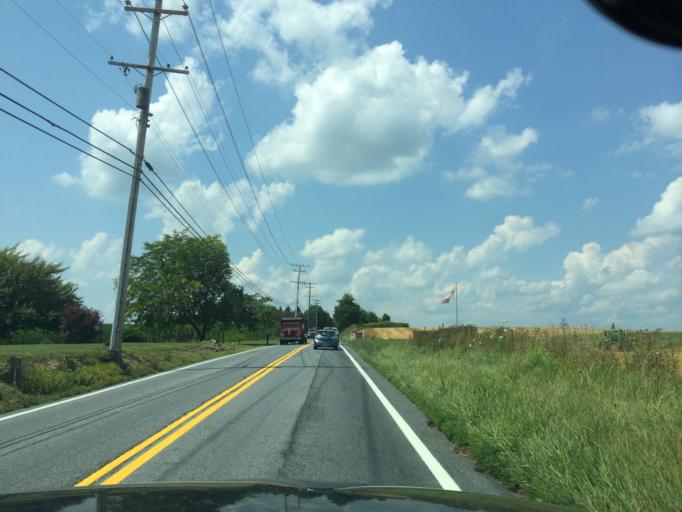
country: US
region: Maryland
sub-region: Carroll County
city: Sykesville
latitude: 39.3754
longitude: -77.0174
